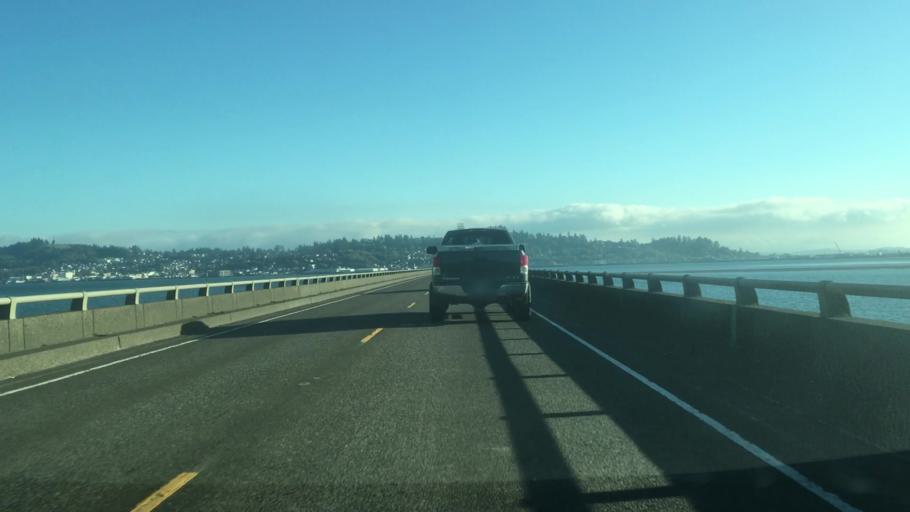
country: US
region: Oregon
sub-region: Clatsop County
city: Astoria
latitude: 46.2129
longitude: -123.8609
